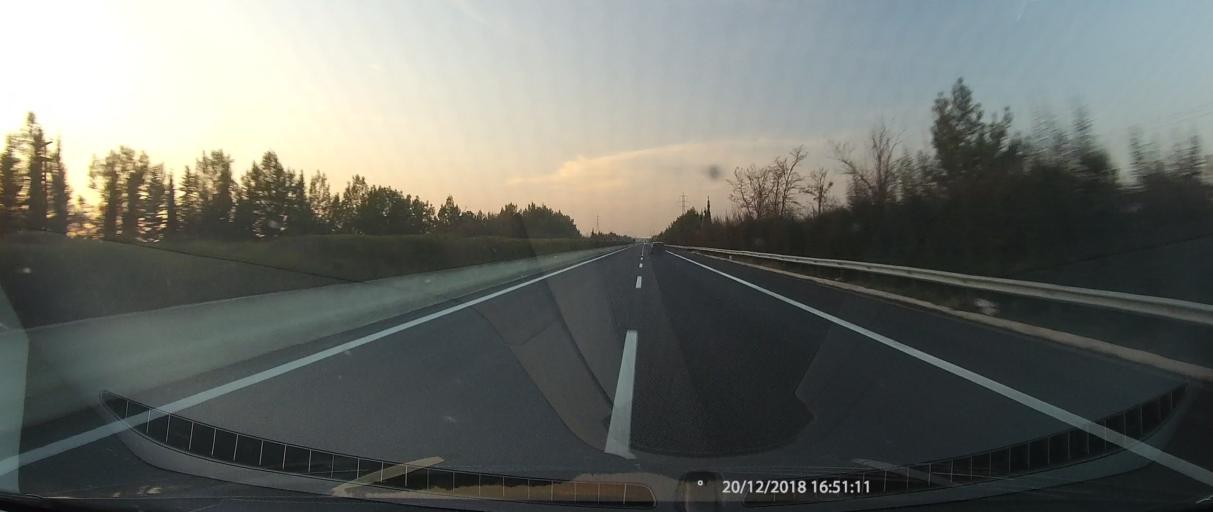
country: GR
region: Thessaly
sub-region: Nomos Larisis
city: Chalki
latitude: 39.5125
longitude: 22.5722
